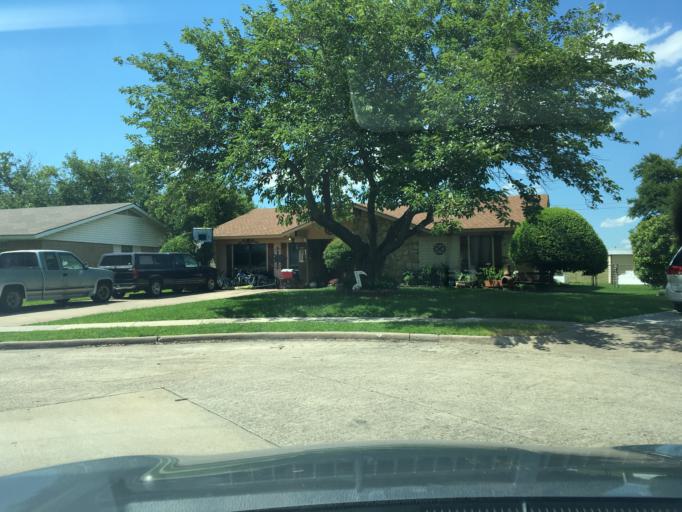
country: US
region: Texas
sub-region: Dallas County
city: Richardson
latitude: 32.9501
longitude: -96.7014
